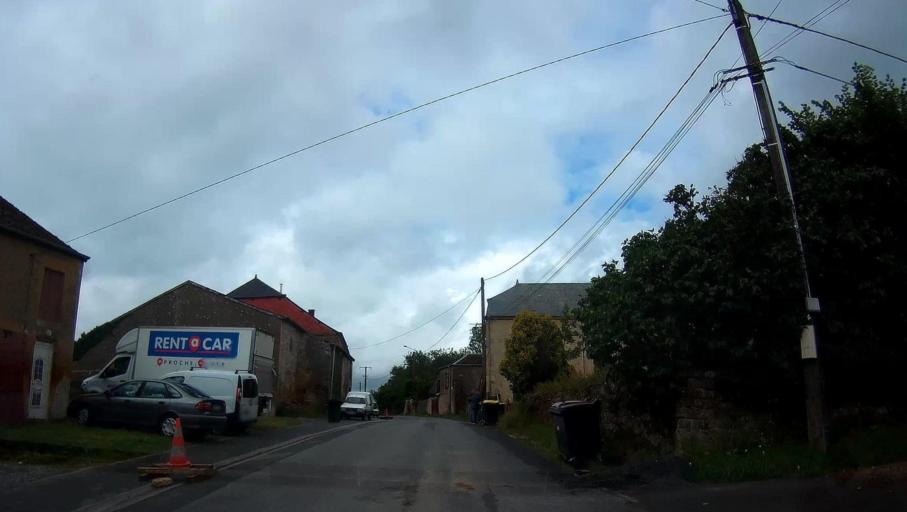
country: FR
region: Champagne-Ardenne
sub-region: Departement des Ardennes
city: Rimogne
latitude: 49.7614
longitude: 4.5064
